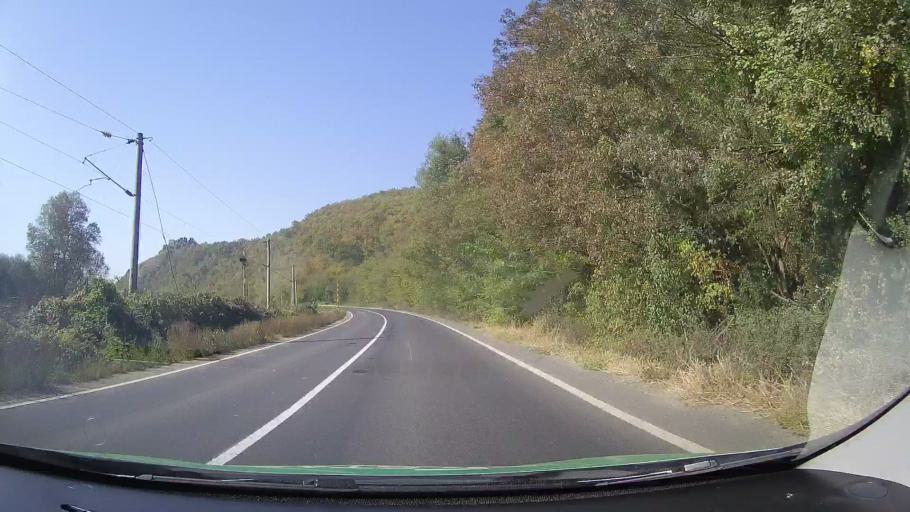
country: RO
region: Arad
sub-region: Oras Lipova
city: Lipova
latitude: 46.1086
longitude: 21.7355
